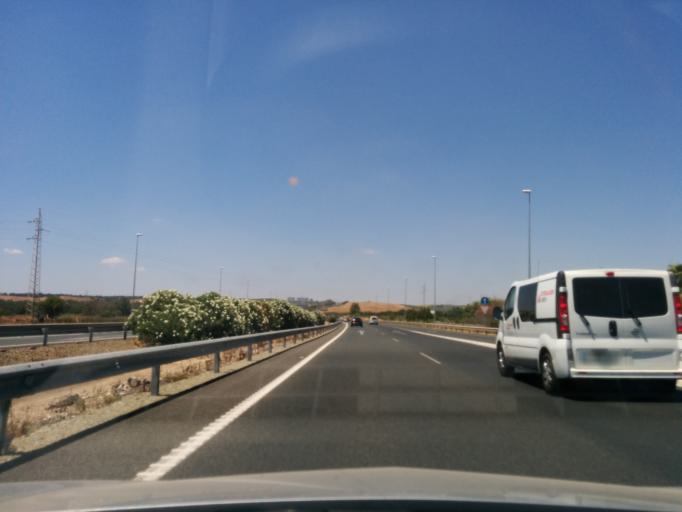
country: ES
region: Andalusia
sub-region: Provincia de Sevilla
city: Carrion de los Cespedes
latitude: 37.3592
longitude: -6.3278
